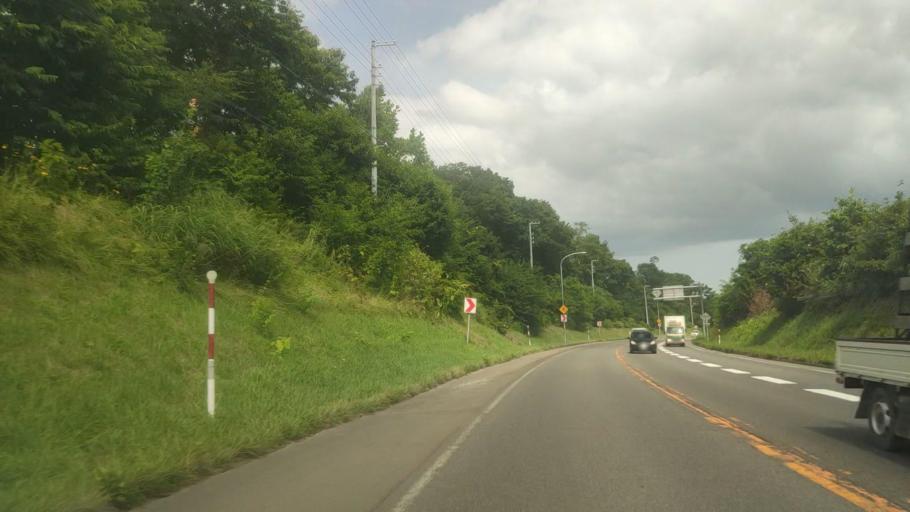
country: JP
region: Hokkaido
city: Nanae
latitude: 42.0560
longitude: 140.5968
